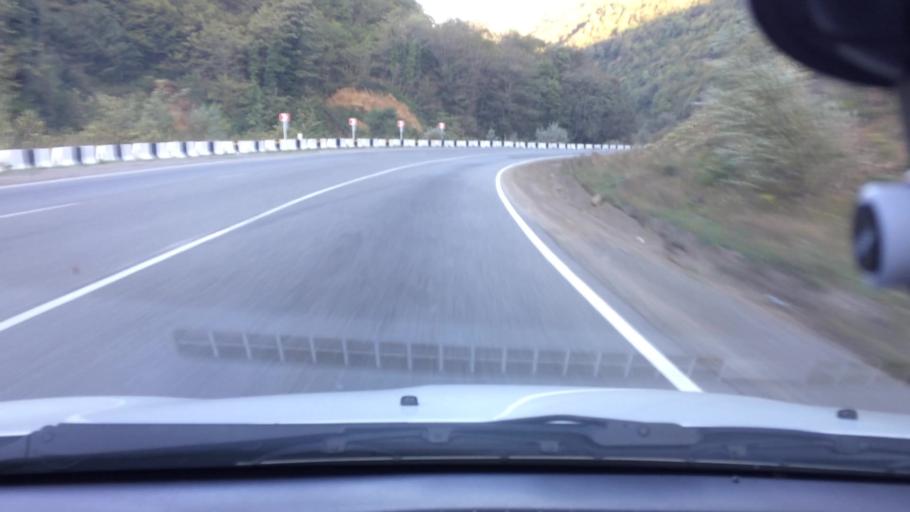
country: GE
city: Surami
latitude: 42.0897
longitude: 43.4642
